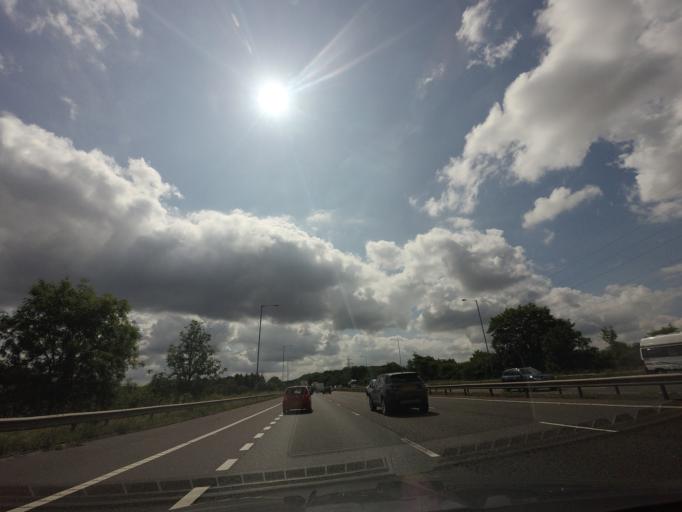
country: GB
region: England
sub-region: St. Helens
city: Billinge
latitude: 53.5293
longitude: -2.6984
